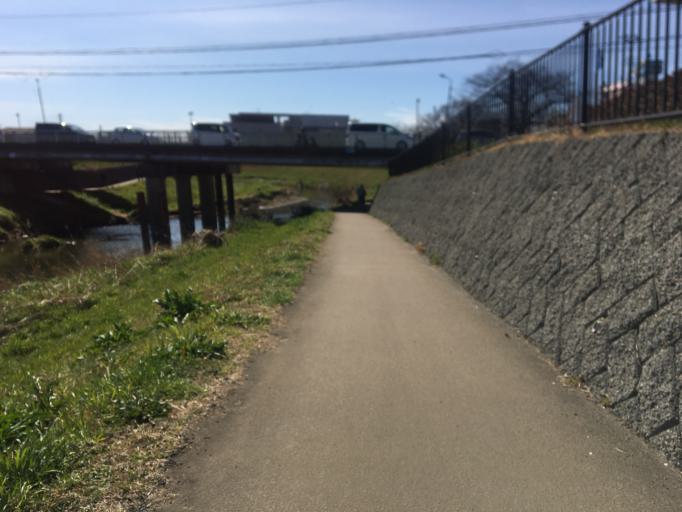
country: JP
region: Saitama
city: Asaka
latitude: 35.8152
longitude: 139.5921
